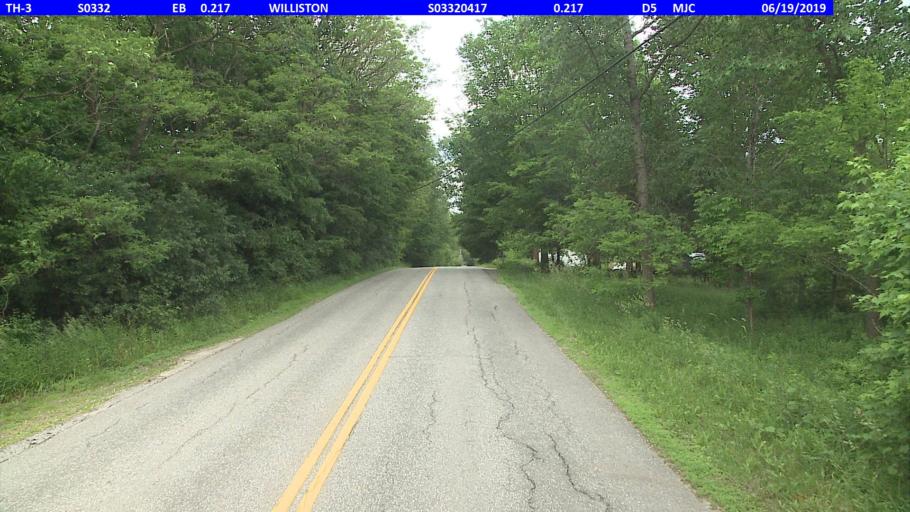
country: US
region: Vermont
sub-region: Chittenden County
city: Williston
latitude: 44.4267
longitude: -73.1174
